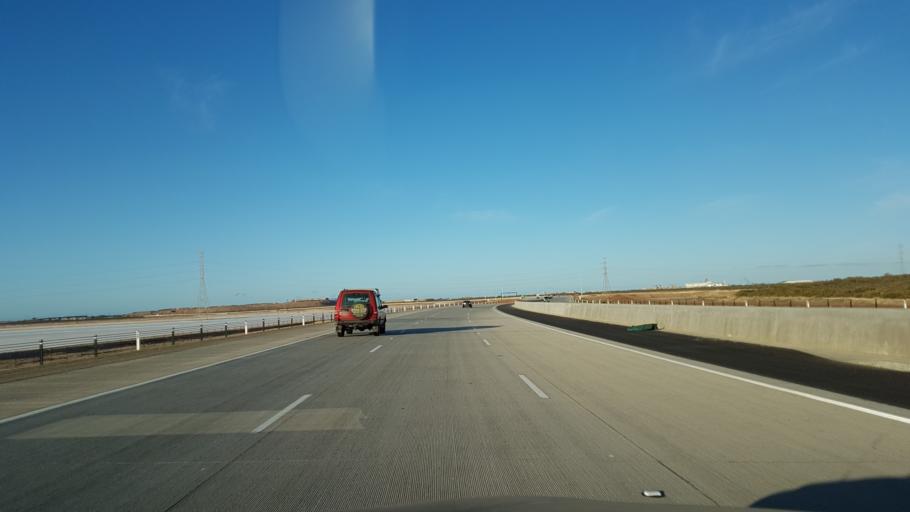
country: AU
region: South Australia
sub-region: Port Adelaide Enfield
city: Enfield
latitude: -34.8063
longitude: 138.5724
